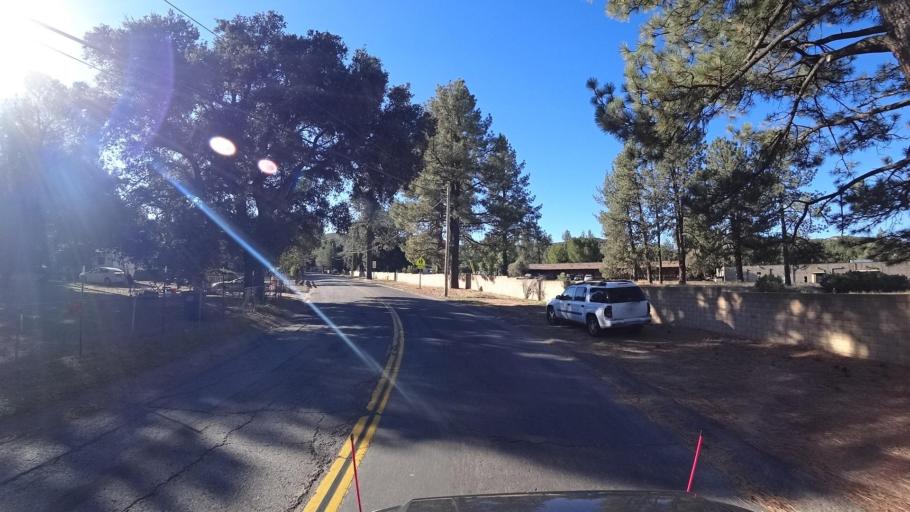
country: US
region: California
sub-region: San Diego County
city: Pine Valley
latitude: 32.8221
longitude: -116.5263
